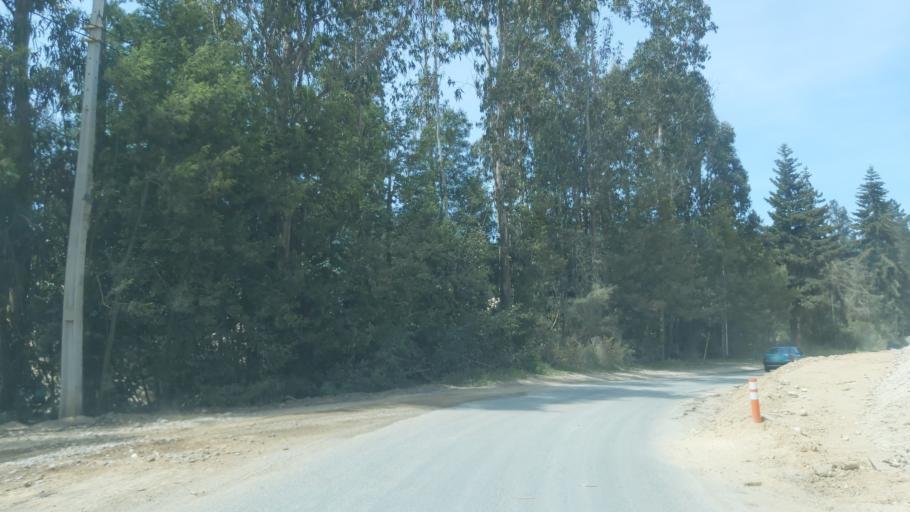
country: CL
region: Maule
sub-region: Provincia de Talca
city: Constitucion
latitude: -35.3869
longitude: -72.4243
